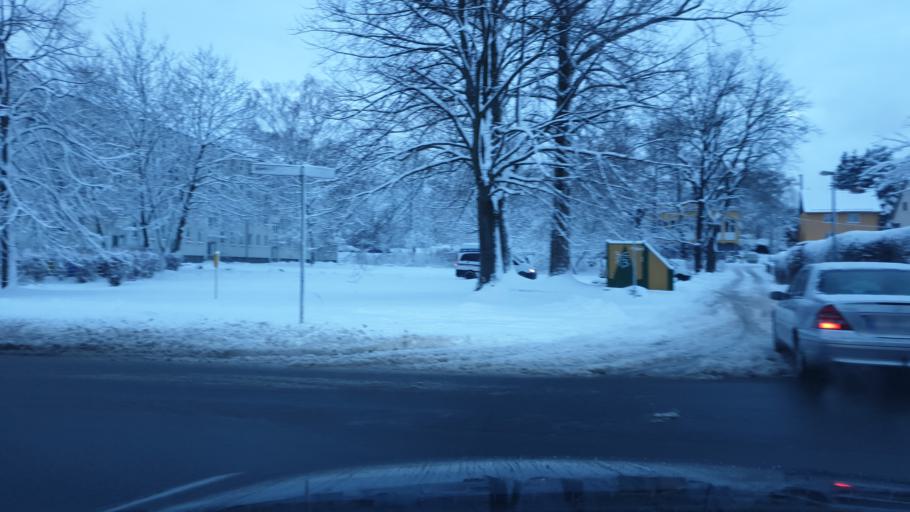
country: DE
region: Saxony
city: Chemnitz
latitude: 50.8563
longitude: 12.9169
